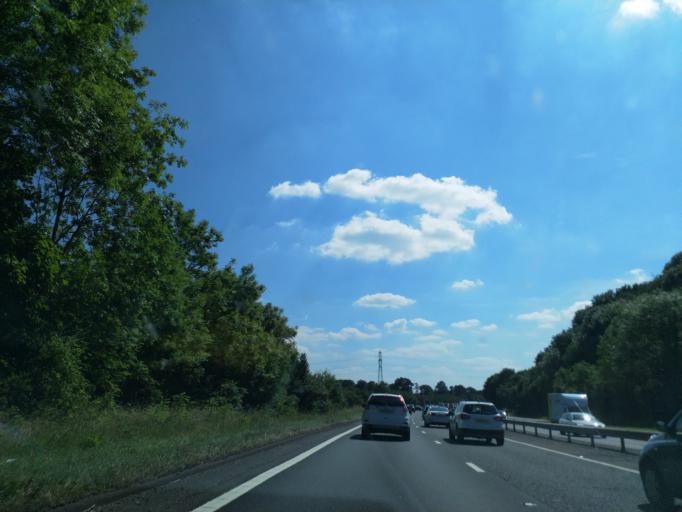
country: GB
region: England
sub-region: Warwickshire
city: Warwick
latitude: 52.3063
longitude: -1.5746
